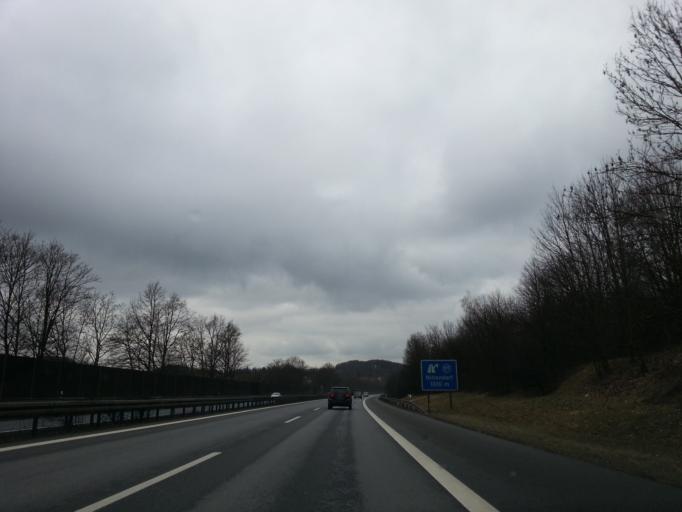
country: DE
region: Bavaria
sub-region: Upper Palatinate
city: Nittendorf
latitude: 49.0211
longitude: 11.9636
